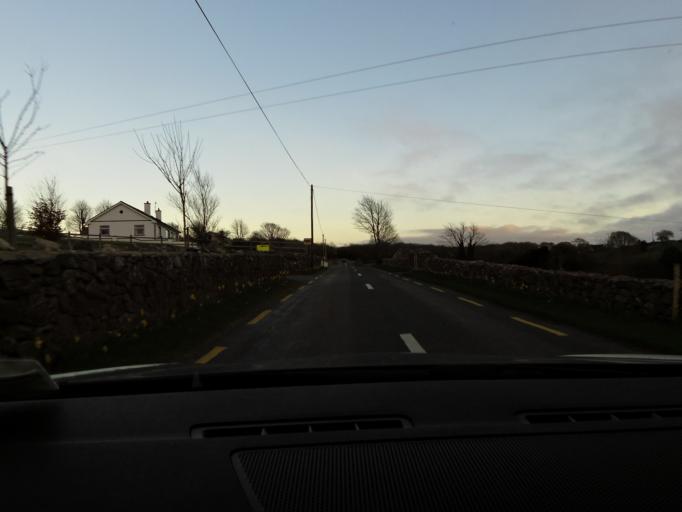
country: IE
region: Connaught
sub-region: Sligo
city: Ballymote
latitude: 53.9753
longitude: -8.4508
